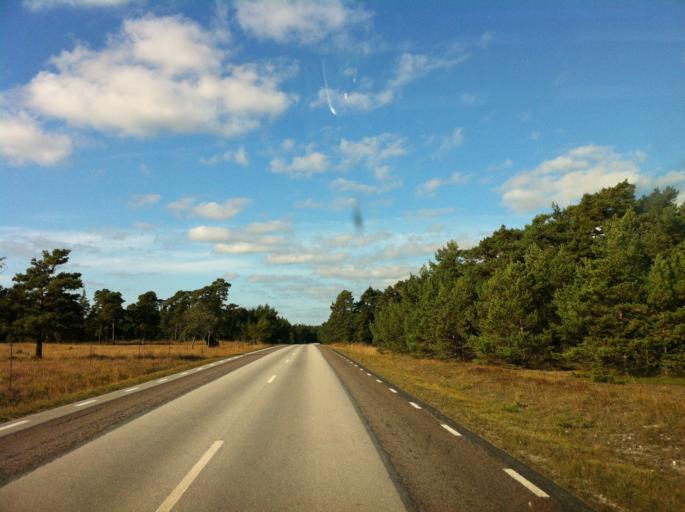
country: SE
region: Gotland
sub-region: Gotland
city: Slite
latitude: 57.4278
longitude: 18.8001
